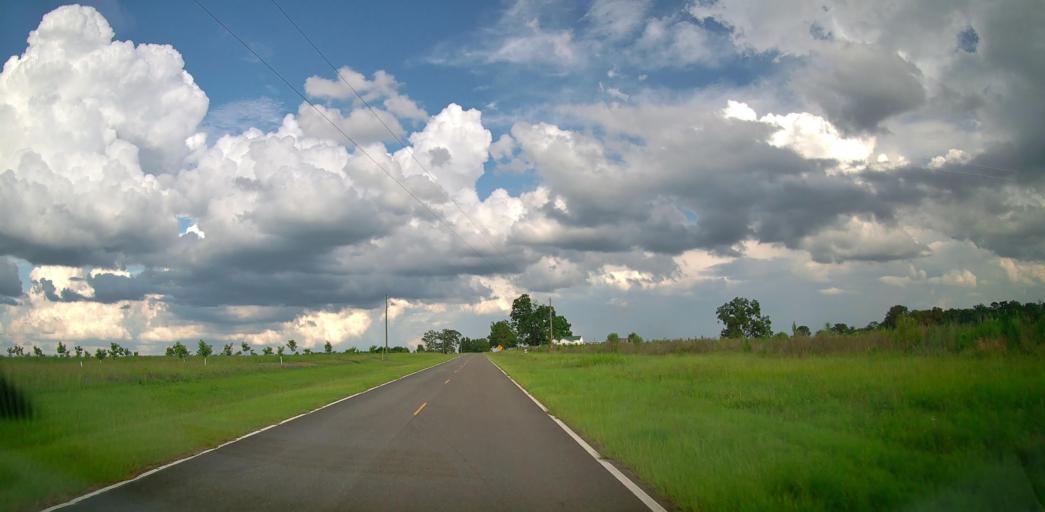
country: US
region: Georgia
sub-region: Bleckley County
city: Cochran
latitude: 32.4098
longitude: -83.4301
